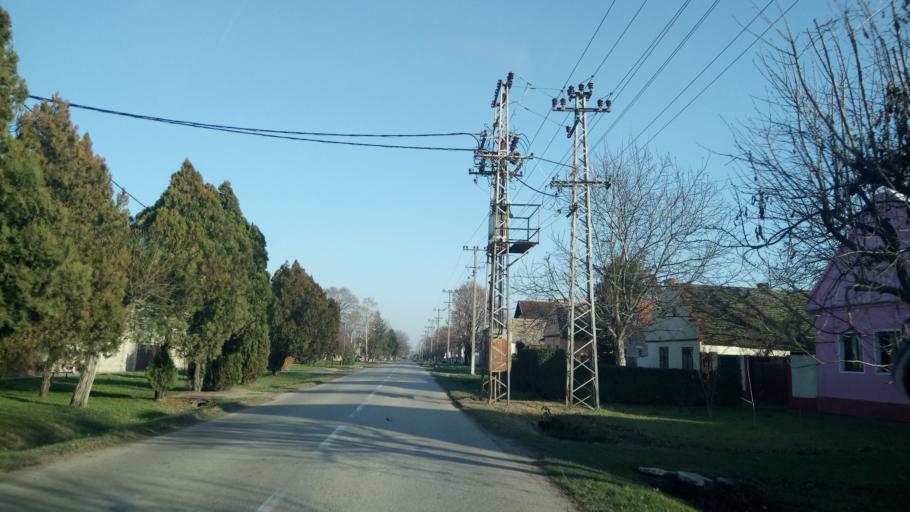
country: RS
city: Krcedin
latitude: 45.1407
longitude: 20.1255
